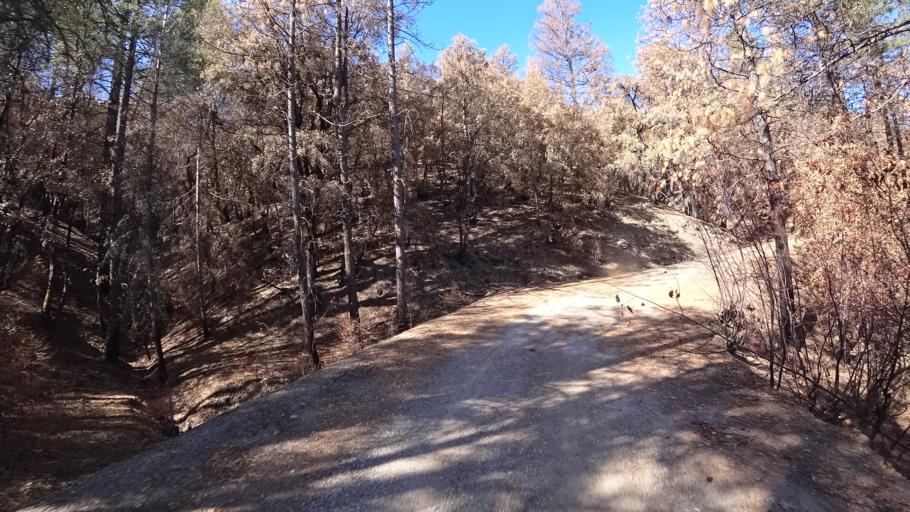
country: US
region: California
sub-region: Tehama County
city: Rancho Tehama Reserve
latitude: 39.6755
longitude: -122.7015
